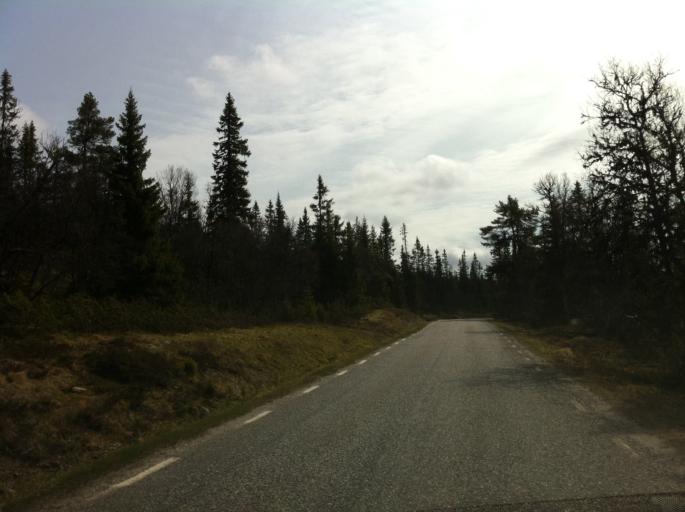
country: NO
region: Hedmark
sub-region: Engerdal
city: Engerdal
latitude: 62.3024
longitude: 12.8010
